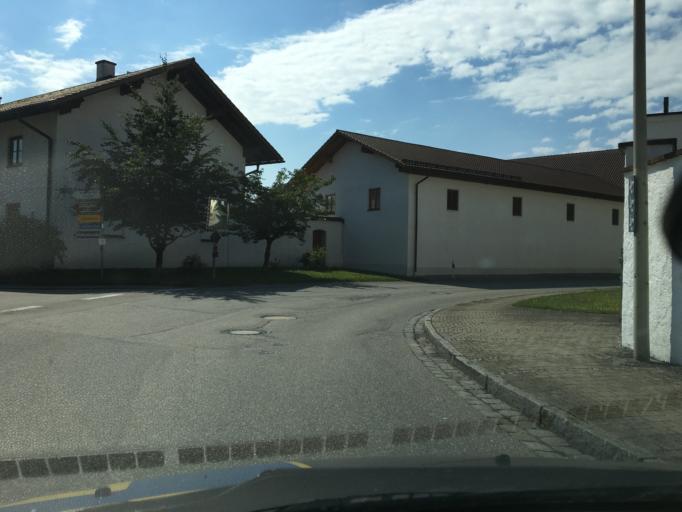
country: DE
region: Bavaria
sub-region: Upper Bavaria
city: Erharting
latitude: 48.2770
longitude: 12.5761
